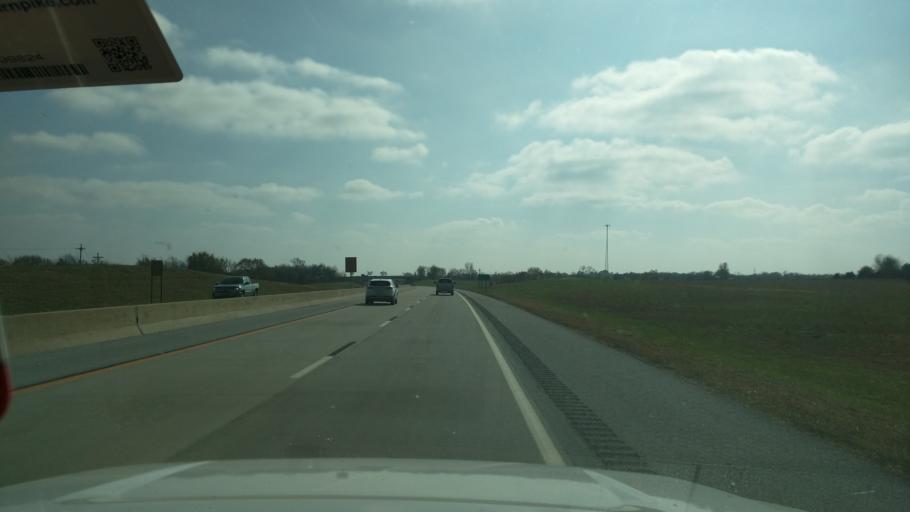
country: US
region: Oklahoma
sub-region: Wagoner County
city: Coweta
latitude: 35.9364
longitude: -95.5853
